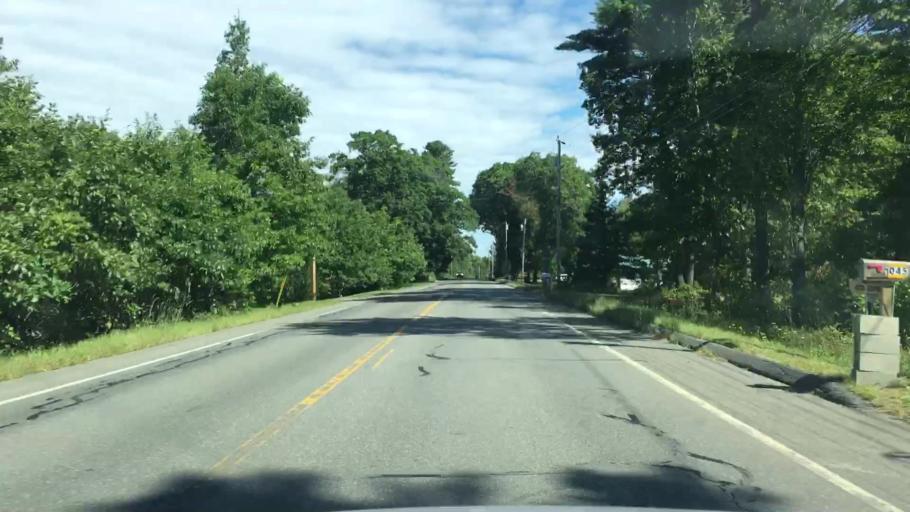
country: US
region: Maine
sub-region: Penobscot County
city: Garland
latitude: 45.0835
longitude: -69.2278
